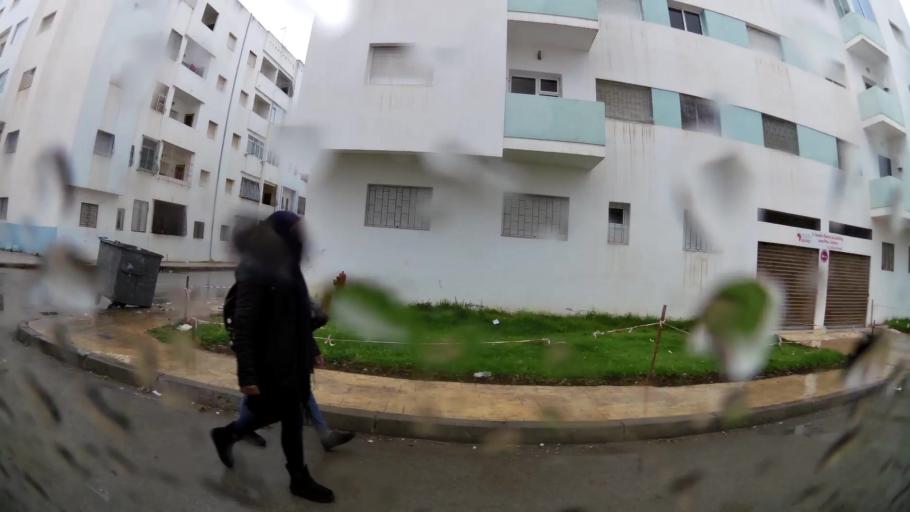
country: MA
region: Tanger-Tetouan
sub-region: Tetouan
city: Martil
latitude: 35.6186
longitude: -5.2831
